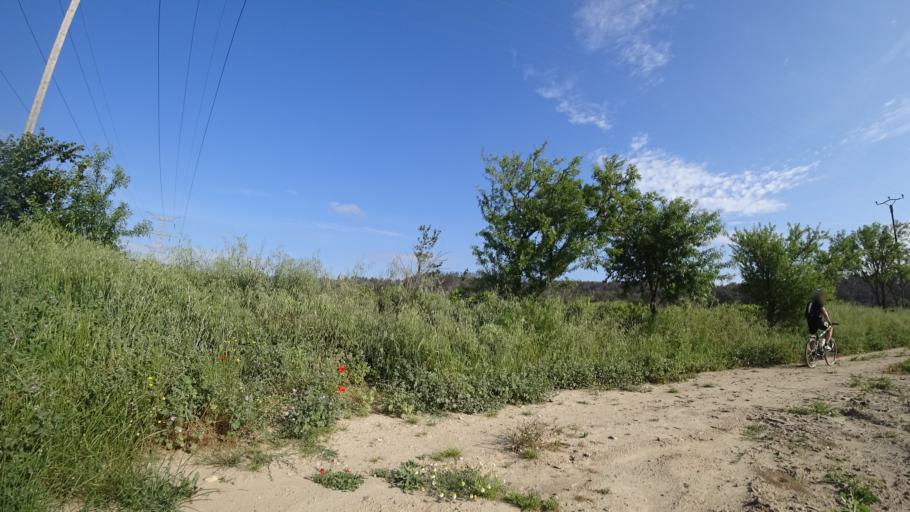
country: FR
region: Languedoc-Roussillon
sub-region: Departement de l'Herault
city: Olonzac
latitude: 43.2386
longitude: 2.7134
